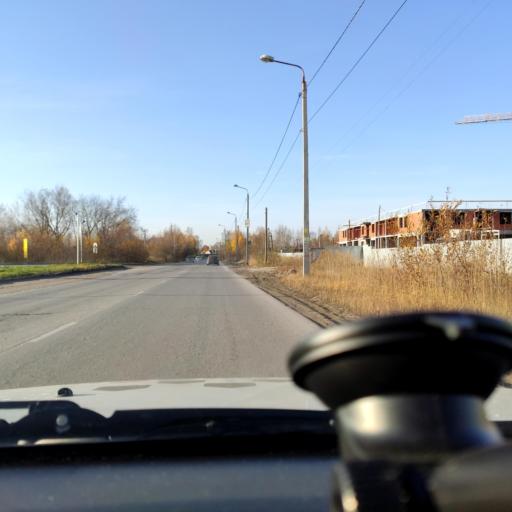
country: RU
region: Perm
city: Perm
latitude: 58.0383
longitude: 56.2609
